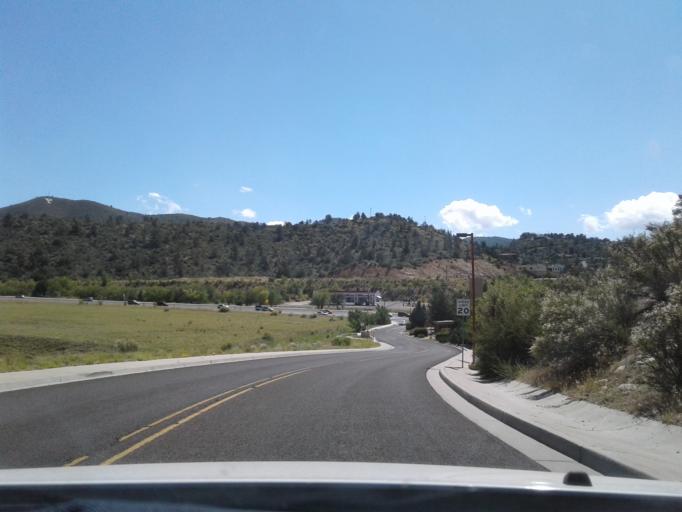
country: US
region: Arizona
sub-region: Yavapai County
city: Prescott
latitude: 34.5504
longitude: -112.4454
